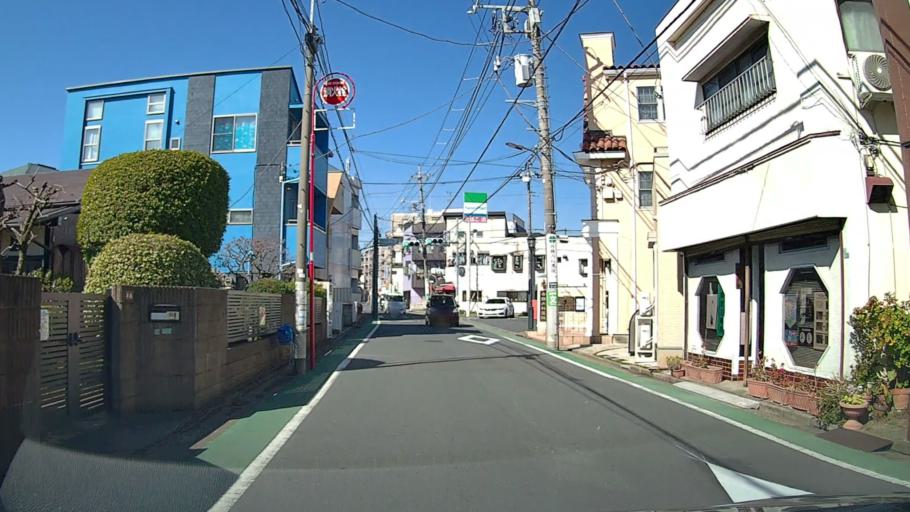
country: JP
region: Saitama
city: Wako
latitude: 35.7472
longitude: 139.5980
